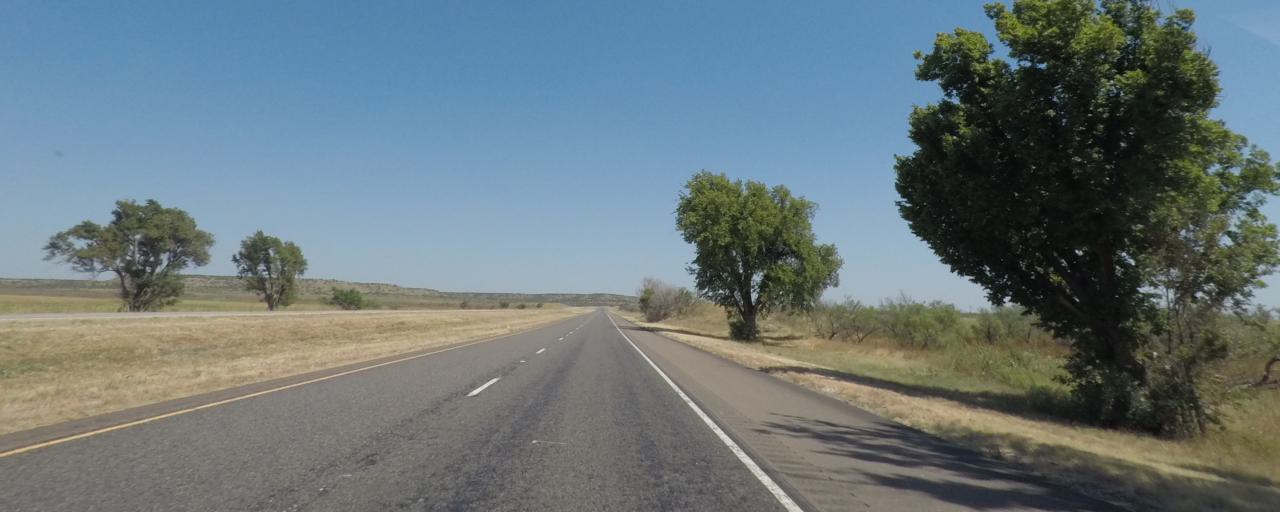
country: US
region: Texas
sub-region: Dickens County
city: Dickens
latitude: 33.6363
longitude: -100.8964
